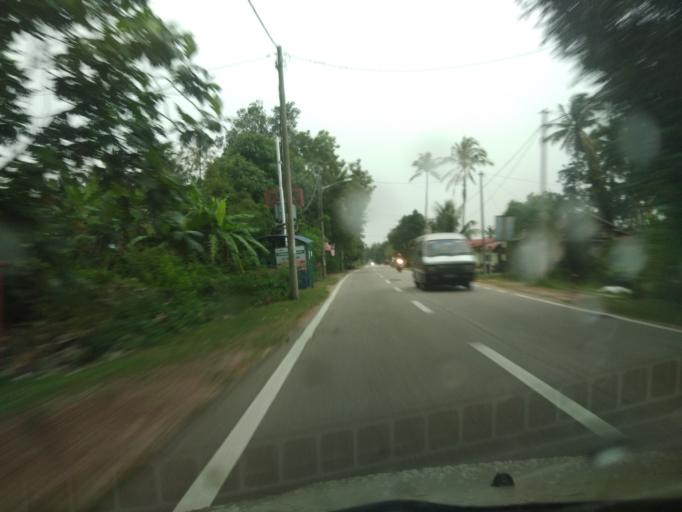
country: MY
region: Penang
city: Kepala Batas
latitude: 5.4996
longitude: 100.3959
